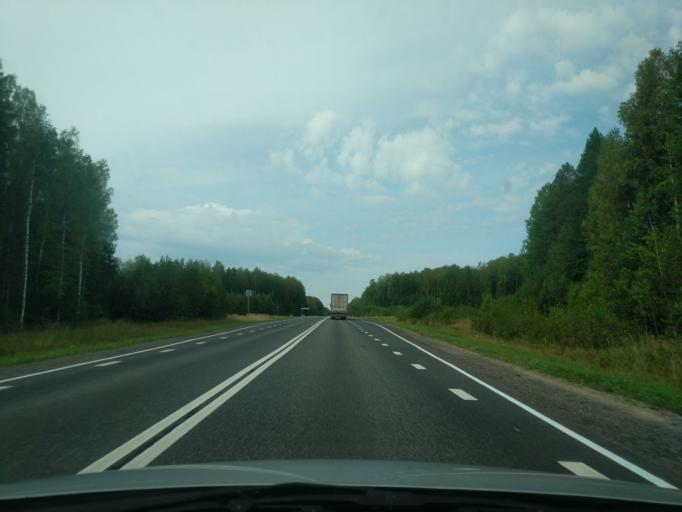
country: RU
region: Kirov
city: Leninskoye
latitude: 58.3189
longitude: 46.8794
